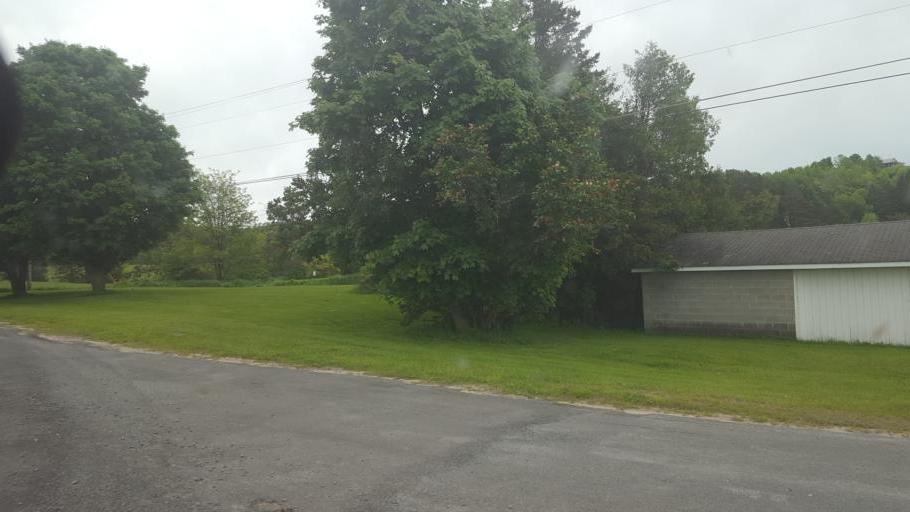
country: US
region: New York
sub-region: Oneida County
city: Chadwicks
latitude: 42.8724
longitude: -75.1709
